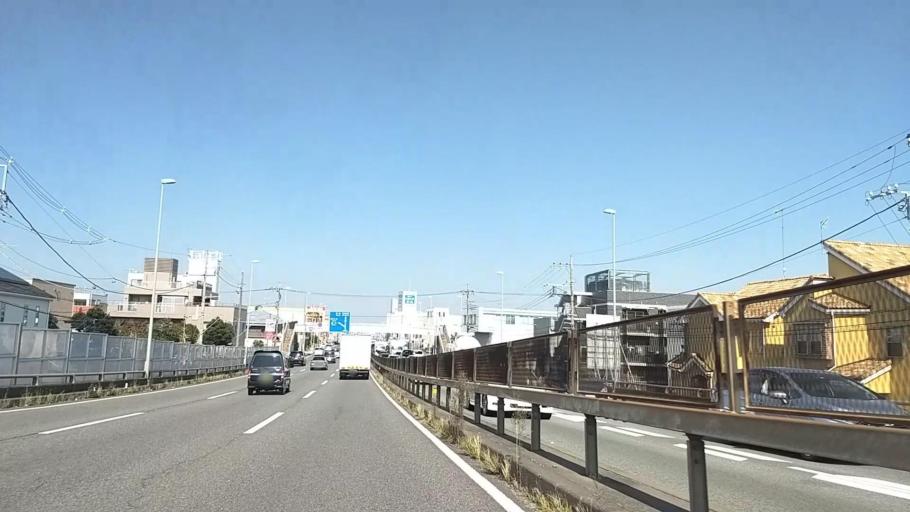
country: JP
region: Kanagawa
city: Atsugi
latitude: 35.4515
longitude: 139.3587
